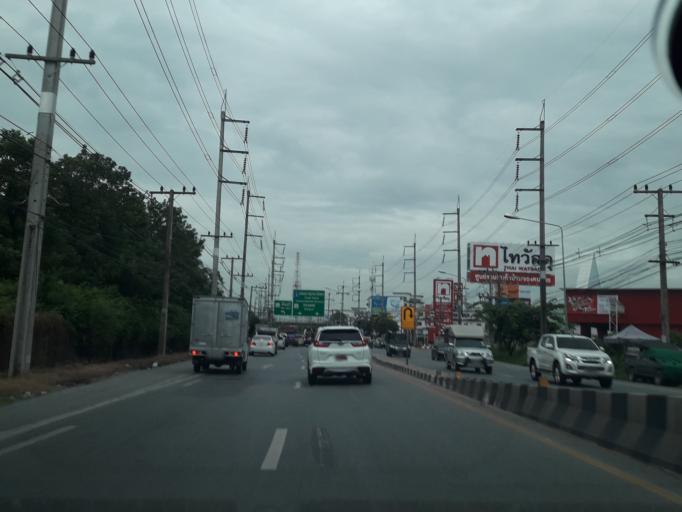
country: TH
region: Pathum Thani
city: Lam Luk Ka
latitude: 13.9376
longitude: 100.7542
